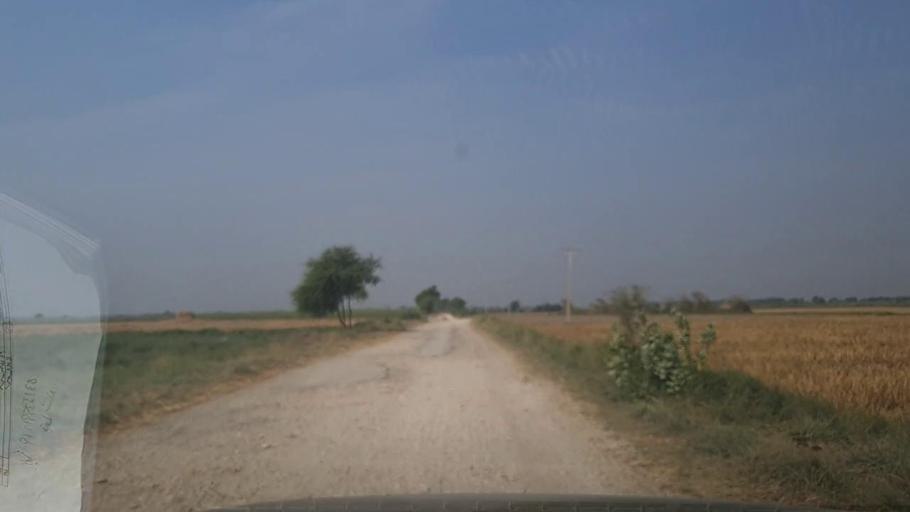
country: PK
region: Sindh
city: Bulri
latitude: 24.9706
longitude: 68.3112
